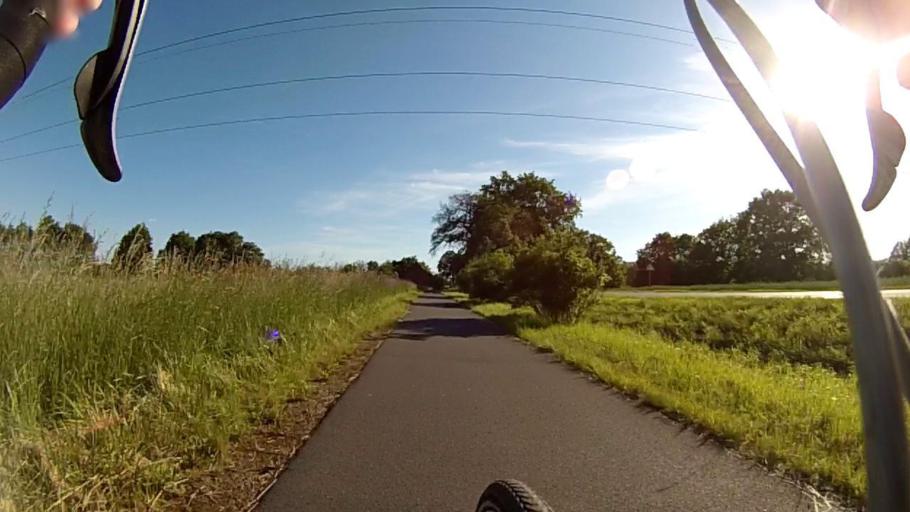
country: DE
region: Brandenburg
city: Ahrensfelde
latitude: 52.6123
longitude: 13.6527
